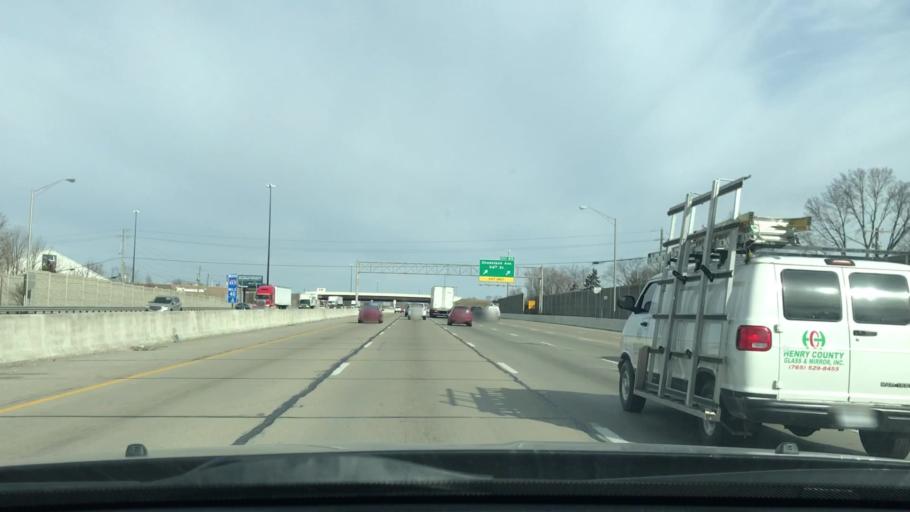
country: US
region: Indiana
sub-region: Marion County
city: Lawrence
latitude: 39.8431
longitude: -86.0418
